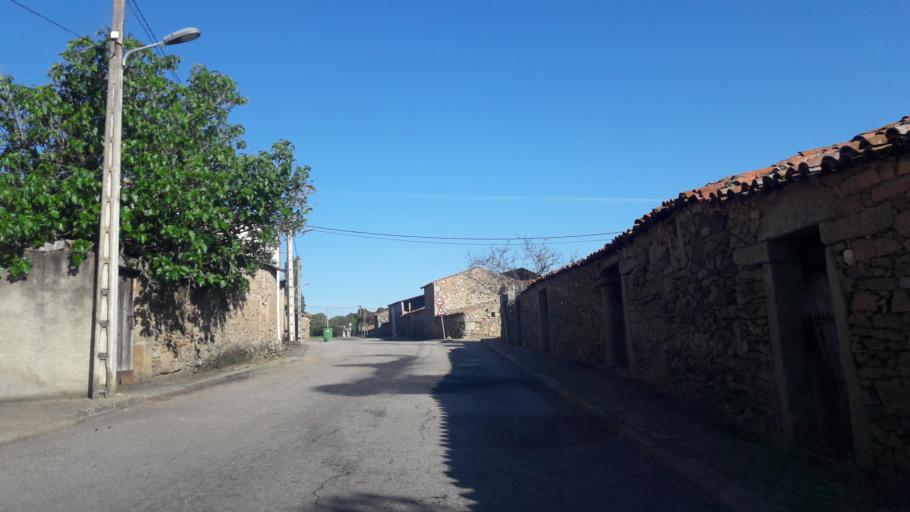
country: ES
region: Castille and Leon
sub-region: Provincia de Salamanca
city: Bogajo
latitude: 40.9065
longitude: -6.5326
